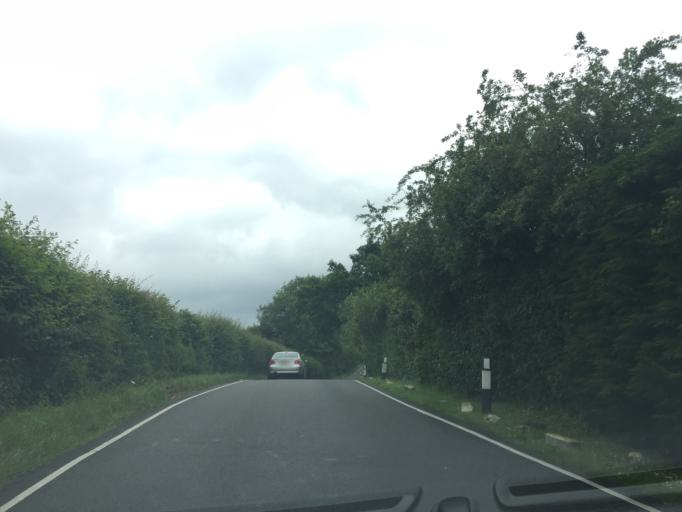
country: GB
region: England
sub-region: Essex
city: Epping
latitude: 51.7366
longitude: 0.1086
